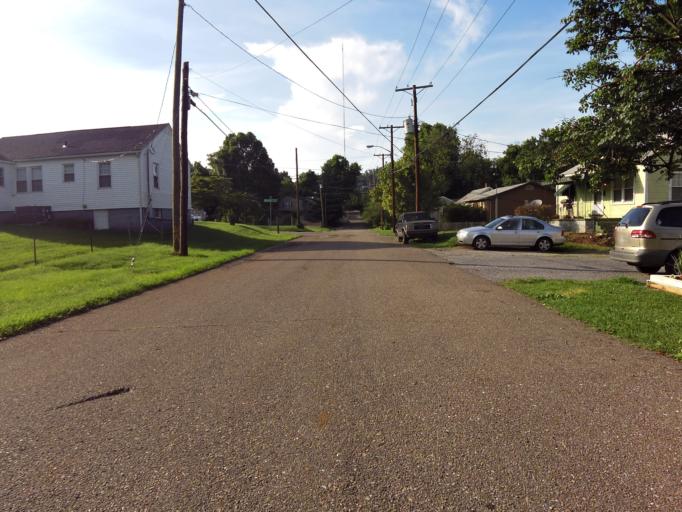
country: US
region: Tennessee
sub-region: Knox County
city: Knoxville
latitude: 35.9999
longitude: -83.9293
